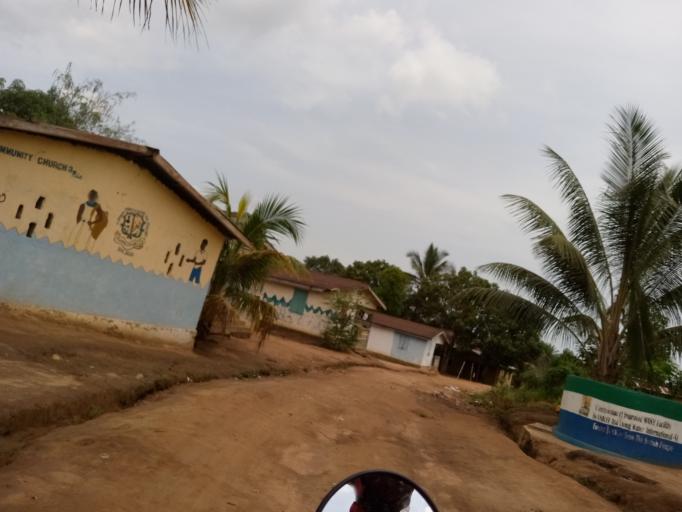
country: SL
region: Western Area
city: Waterloo
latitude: 8.3330
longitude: -13.0218
